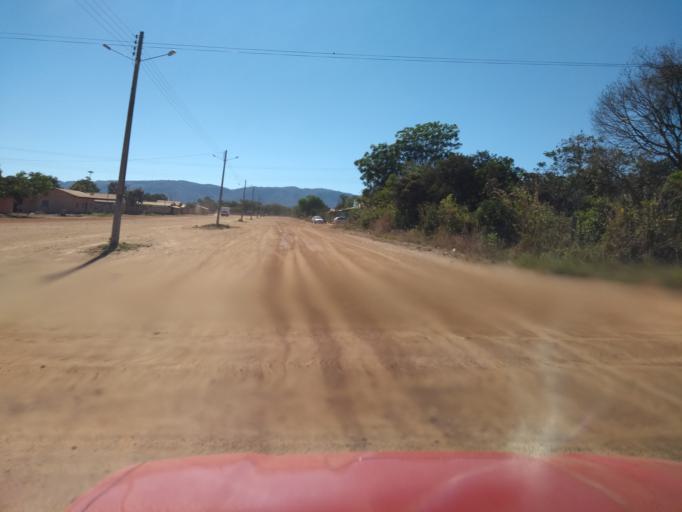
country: BR
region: Goias
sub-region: Cavalcante
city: Cavalcante
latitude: -13.7987
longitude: -47.4439
